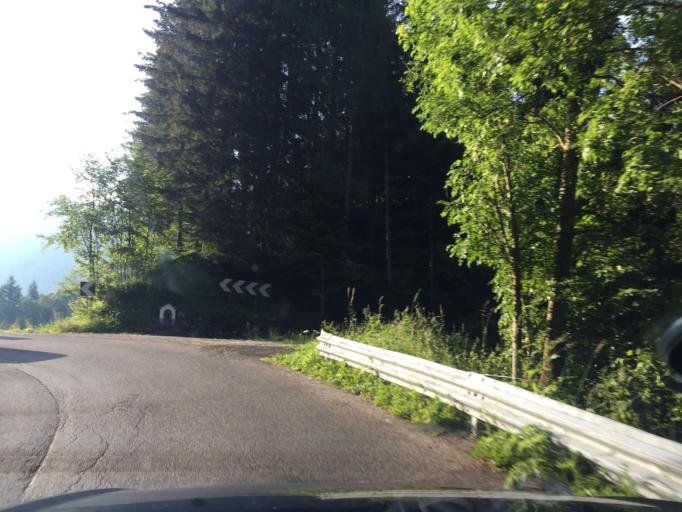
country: IT
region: Friuli Venezia Giulia
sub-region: Provincia di Udine
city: Rigolato
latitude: 46.5812
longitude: 12.8238
